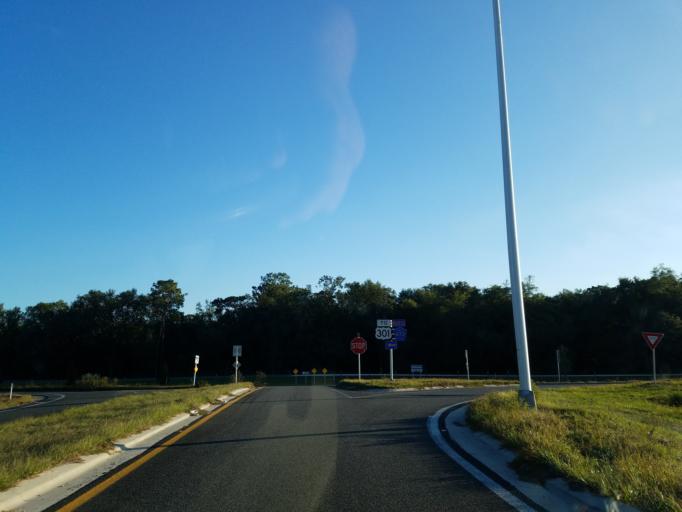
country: US
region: Florida
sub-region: Hernando County
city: Ridge Manor
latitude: 28.6030
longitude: -82.2005
